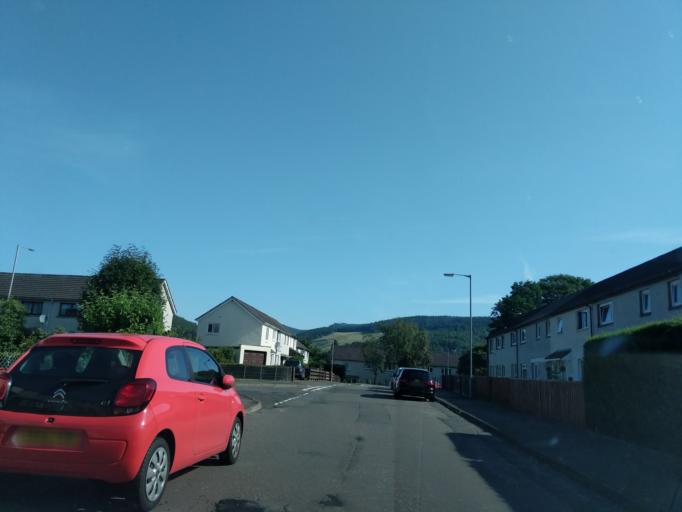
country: GB
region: Scotland
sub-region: The Scottish Borders
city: Peebles
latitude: 55.6436
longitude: -3.1834
